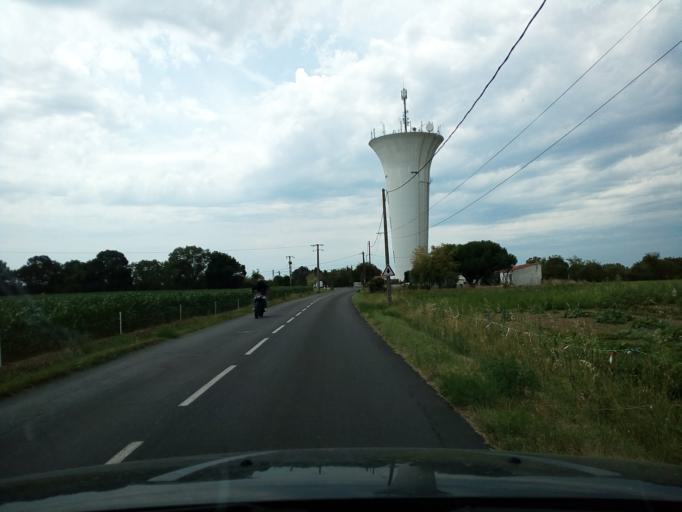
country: FR
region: Poitou-Charentes
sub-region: Departement de la Charente-Maritime
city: Dolus-d'Oleron
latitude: 45.9329
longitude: -1.3145
